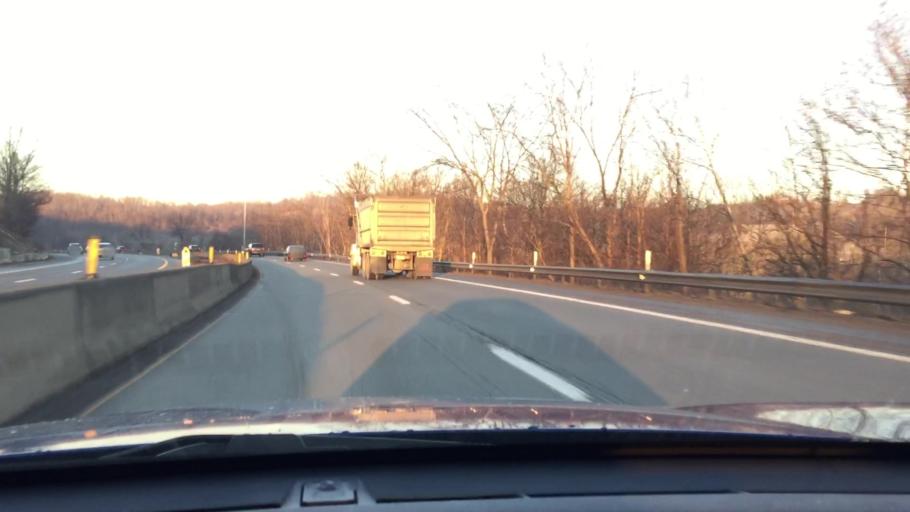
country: US
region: Pennsylvania
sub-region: Washington County
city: East Washington
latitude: 40.1681
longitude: -80.1741
